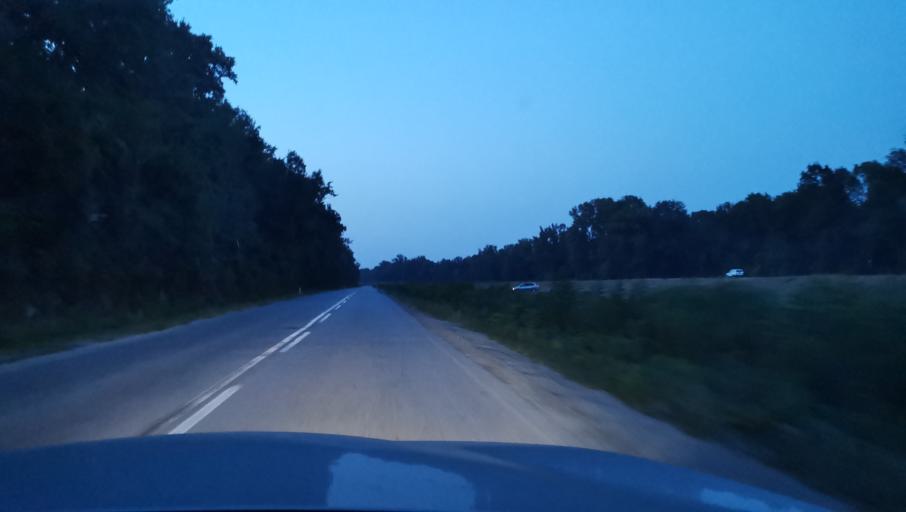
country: RS
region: Central Serbia
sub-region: Belgrade
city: Obrenovac
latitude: 44.6833
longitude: 20.1918
